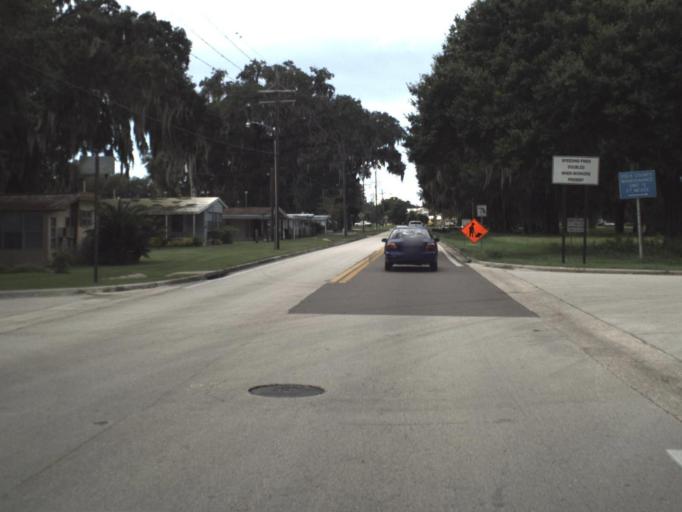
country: US
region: Florida
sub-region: Polk County
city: Fort Meade
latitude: 27.7514
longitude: -81.7845
